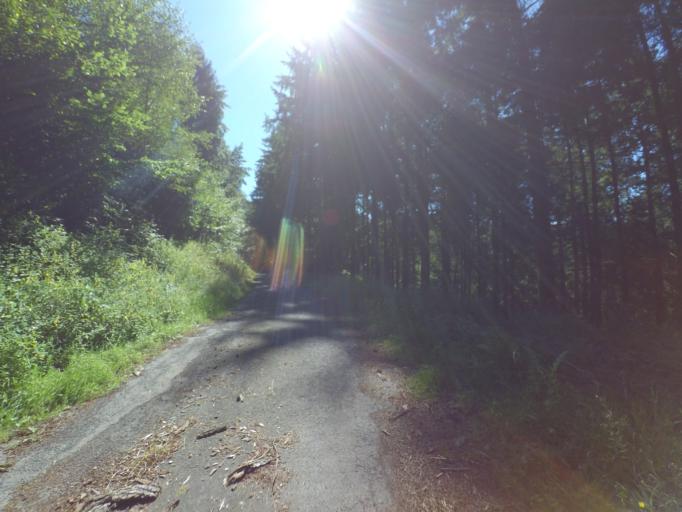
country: DE
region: Rheinland-Pfalz
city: Bad Bertrich
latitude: 50.0562
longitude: 7.0703
